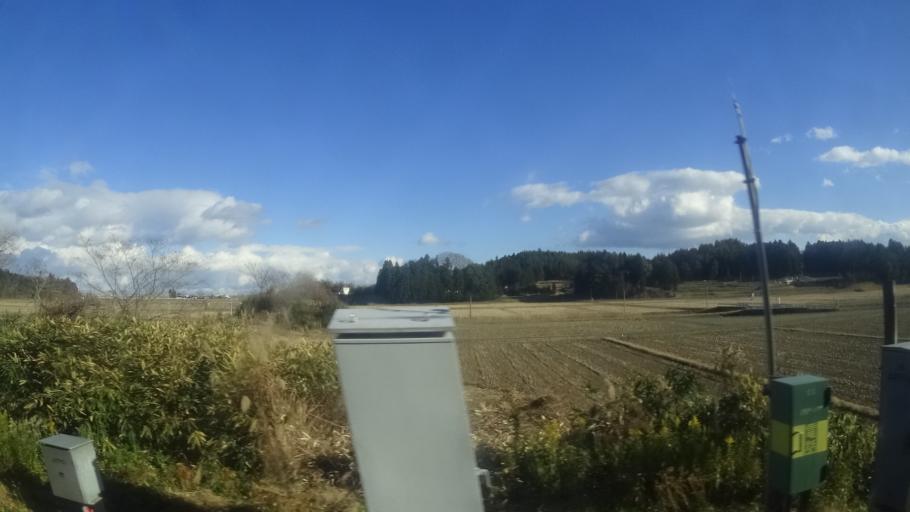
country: JP
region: Fukushima
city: Namie
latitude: 37.6829
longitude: 140.9722
